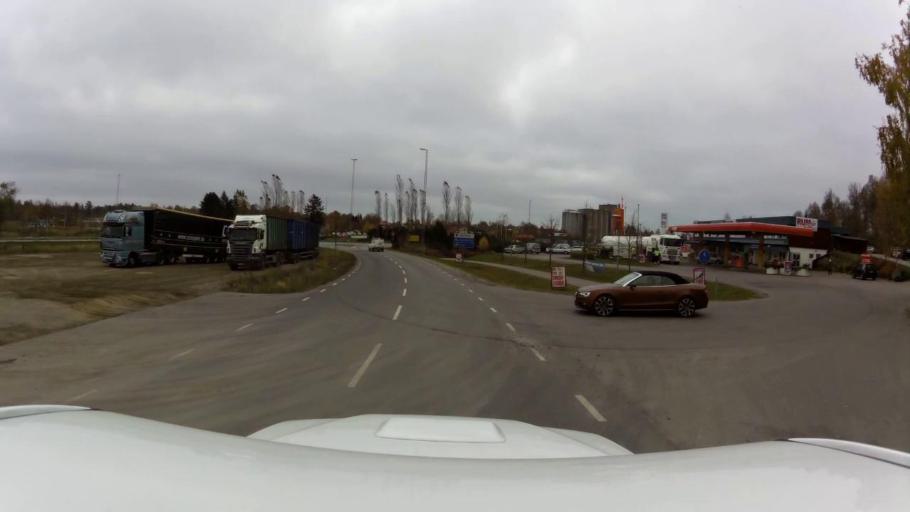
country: SE
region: OEstergoetland
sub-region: Kinda Kommun
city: Rimforsa
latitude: 58.1396
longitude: 15.6791
